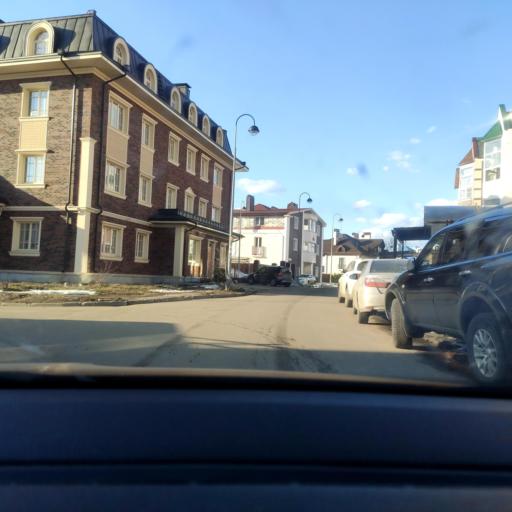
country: RU
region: Moskovskaya
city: Novopodrezkovo
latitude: 55.9040
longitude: 37.3784
